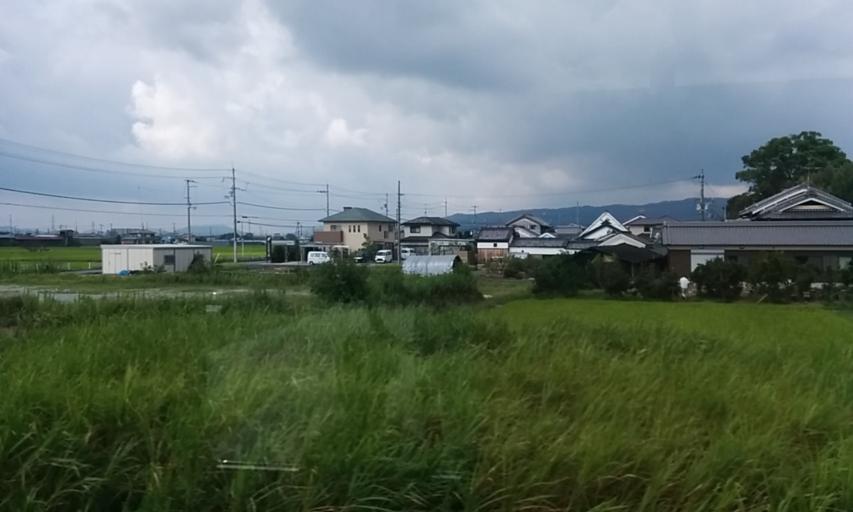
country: JP
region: Nara
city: Nara-shi
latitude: 34.6336
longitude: 135.7808
